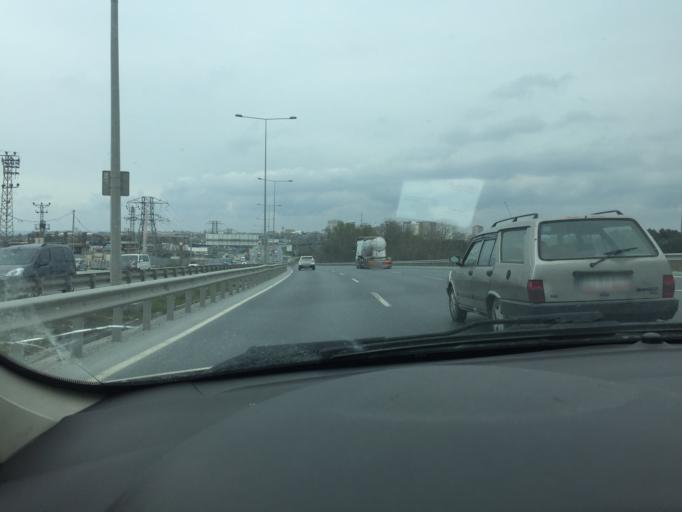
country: TR
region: Istanbul
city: Basaksehir
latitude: 41.1362
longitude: 28.8113
